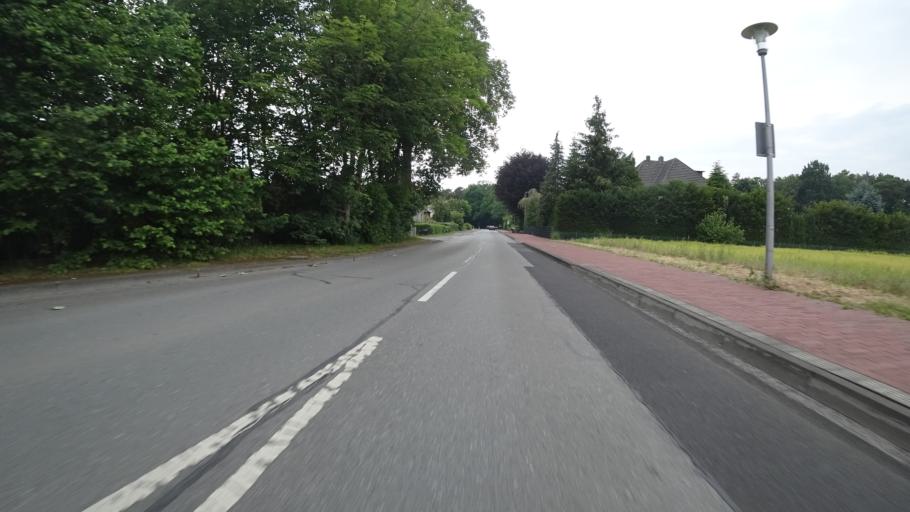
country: DE
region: North Rhine-Westphalia
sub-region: Regierungsbezirk Detmold
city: Guetersloh
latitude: 51.9323
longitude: 8.3828
